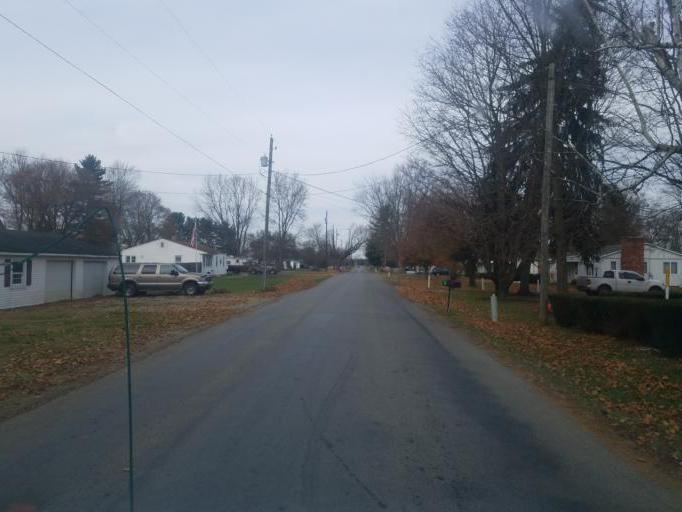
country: US
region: Ohio
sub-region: Knox County
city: Mount Vernon
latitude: 40.3967
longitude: -82.5130
